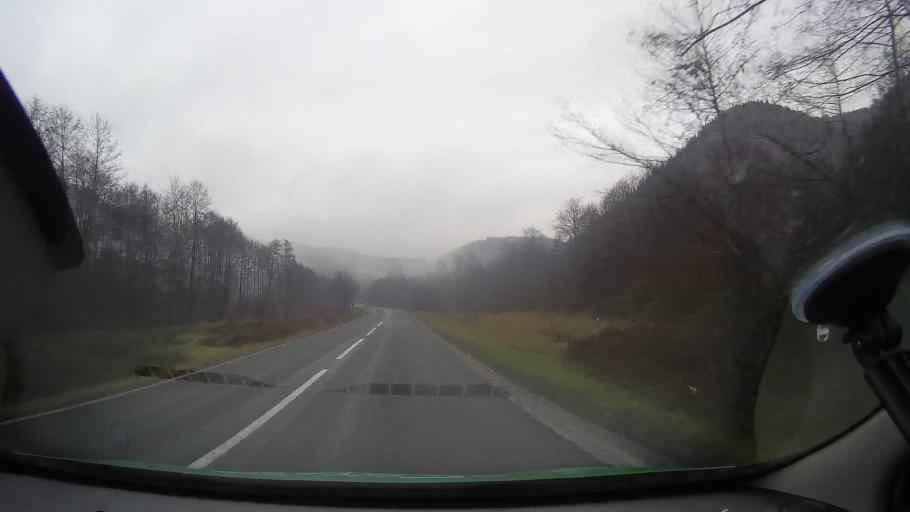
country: RO
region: Arad
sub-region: Comuna Plescuta
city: Plescuta
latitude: 46.3118
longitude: 22.4562
